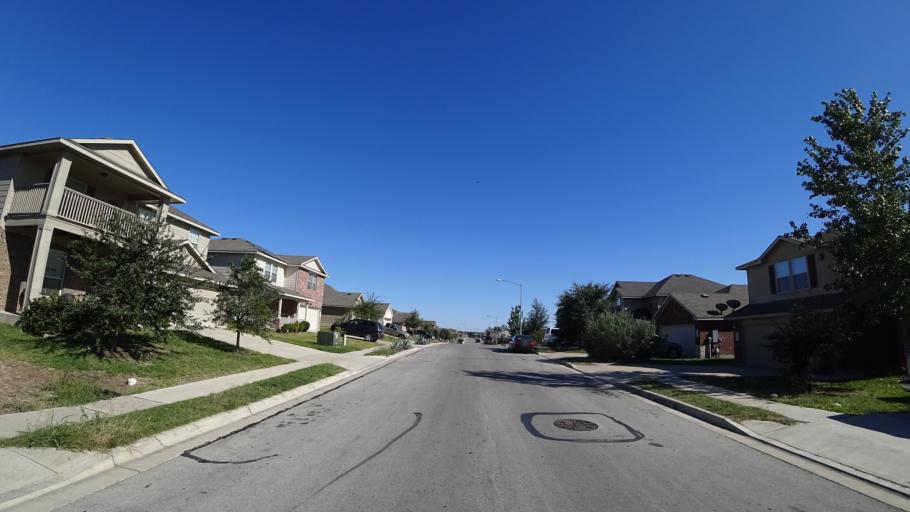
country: US
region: Texas
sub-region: Travis County
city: Hornsby Bend
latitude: 30.2805
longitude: -97.6279
